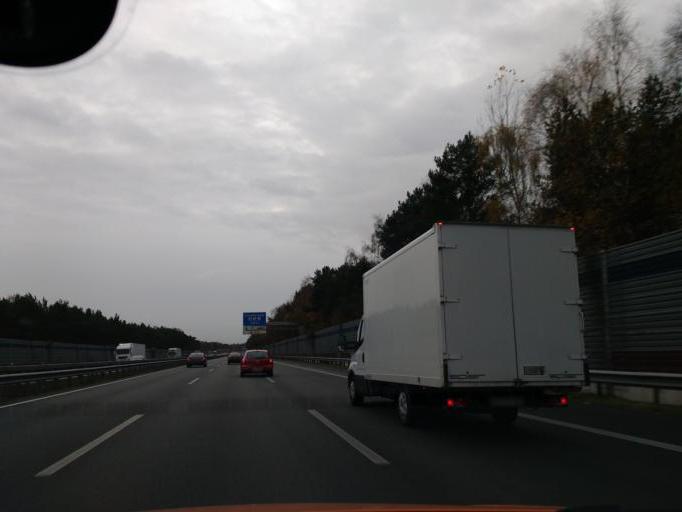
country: DE
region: Lower Saxony
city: Ottersberg
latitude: 53.0973
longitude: 9.1865
